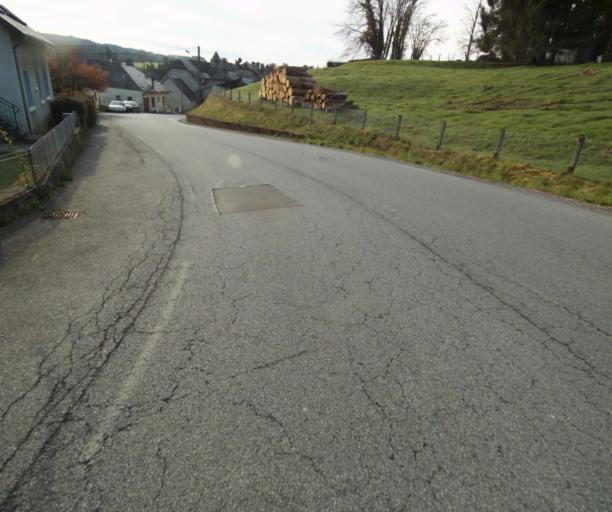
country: FR
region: Limousin
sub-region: Departement de la Correze
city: Correze
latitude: 45.3744
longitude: 1.8730
